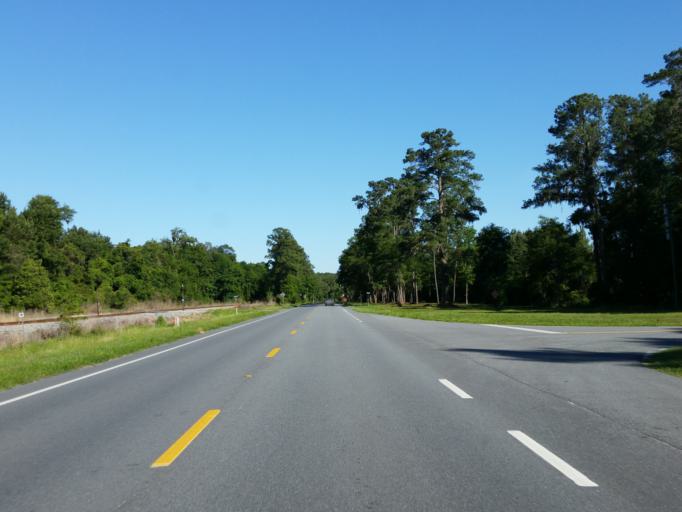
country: US
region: Florida
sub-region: Suwannee County
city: Wellborn
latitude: 30.3445
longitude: -82.7659
